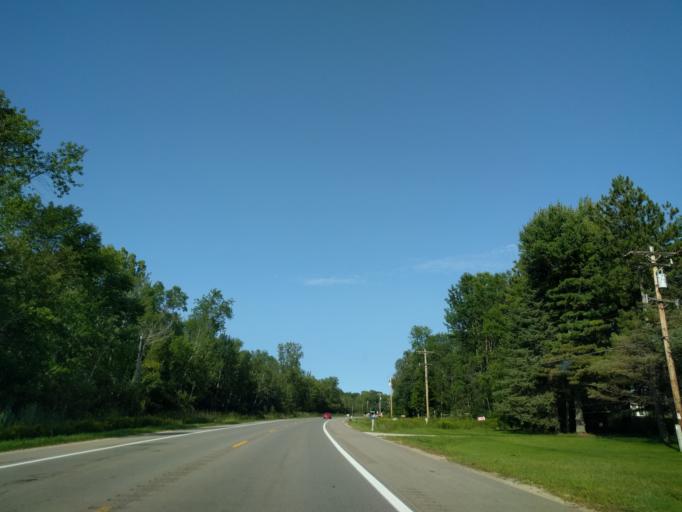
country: US
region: Michigan
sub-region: Menominee County
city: Menominee
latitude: 45.1680
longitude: -87.5854
